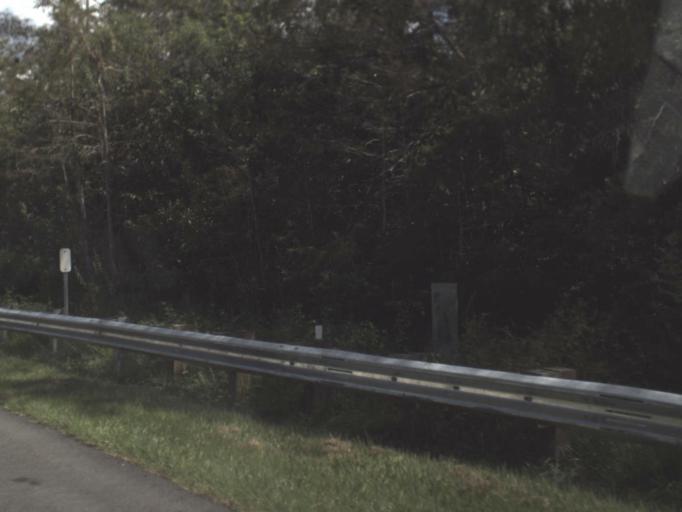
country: US
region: Florida
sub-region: Miami-Dade County
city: Kendall West
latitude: 25.8462
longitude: -80.9276
